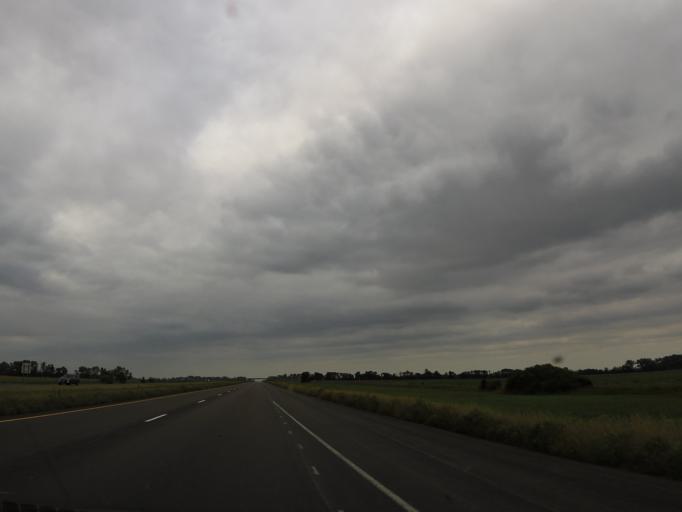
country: US
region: North Dakota
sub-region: Richland County
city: Wahpeton
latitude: 45.9830
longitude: -96.8359
